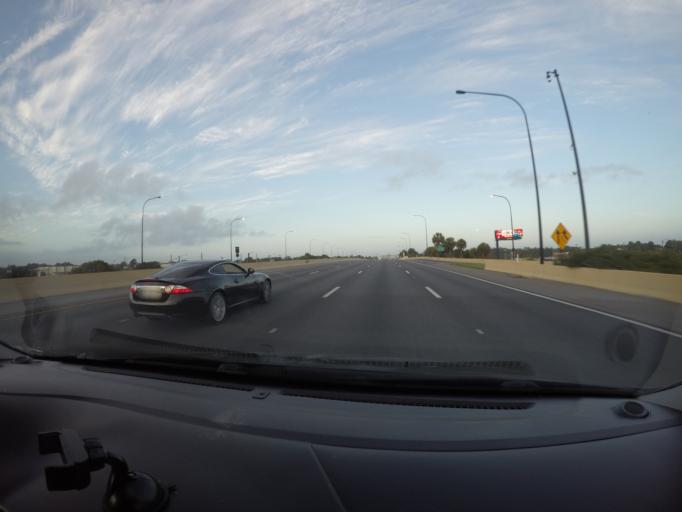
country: US
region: Florida
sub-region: Orange County
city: Azalea Park
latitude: 28.5397
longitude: -81.3094
